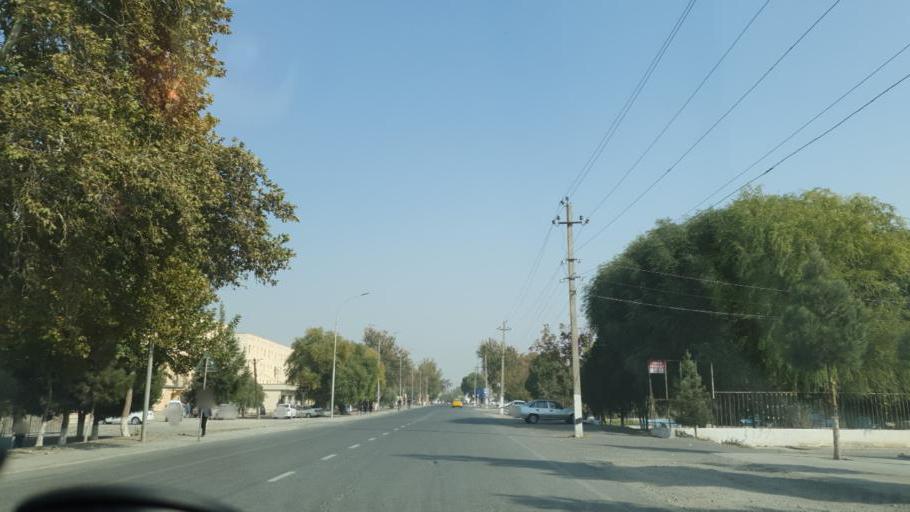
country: UZ
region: Fergana
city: Beshariq
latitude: 40.4342
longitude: 70.5915
